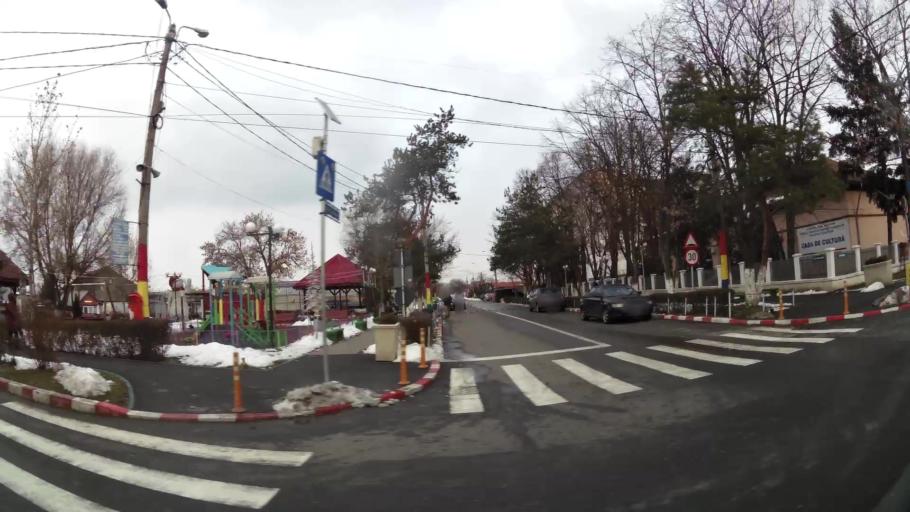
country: RO
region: Ilfov
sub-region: Voluntari City
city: Voluntari
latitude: 44.4884
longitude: 26.1716
